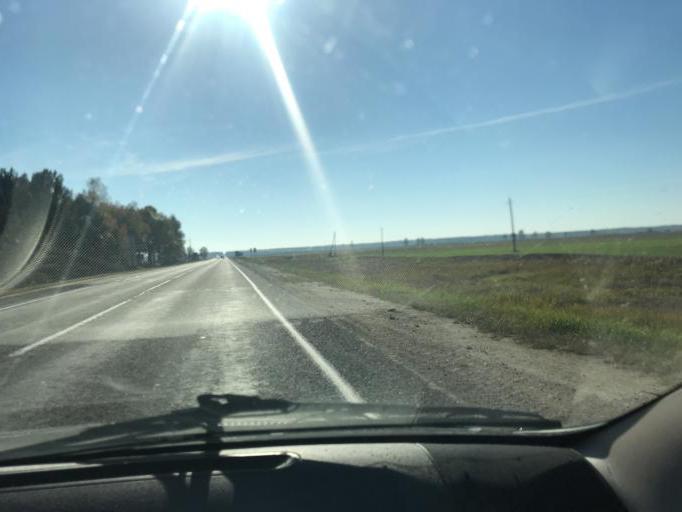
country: BY
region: Minsk
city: Starobin
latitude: 52.5337
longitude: 27.4737
